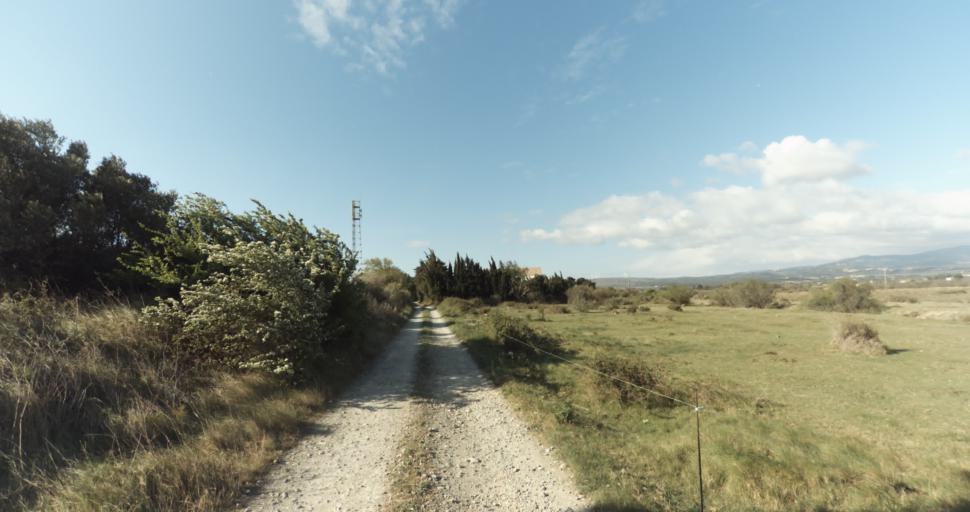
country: FR
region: Languedoc-Roussillon
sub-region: Departement de l'Aude
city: Leucate
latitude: 42.9342
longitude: 3.0131
